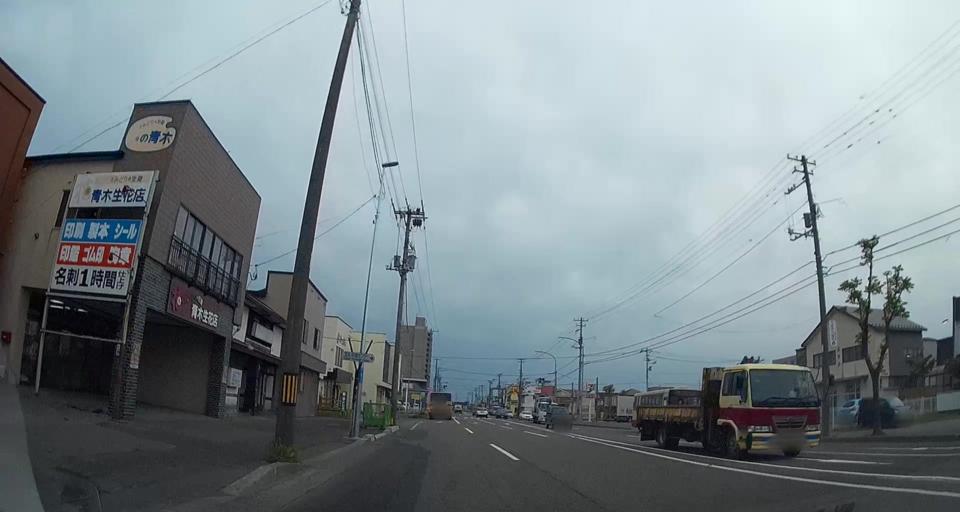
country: JP
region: Hokkaido
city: Tomakomai
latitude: 42.6302
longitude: 141.5968
